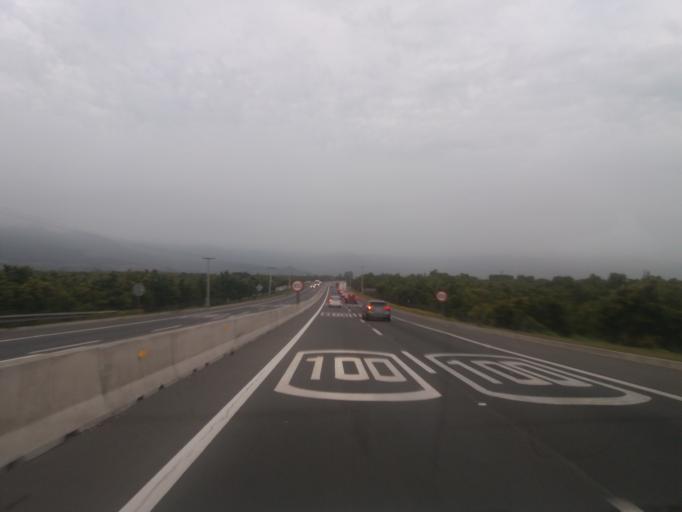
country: CL
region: Valparaiso
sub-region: Provincia de Quillota
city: Hacienda La Calera
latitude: -32.8269
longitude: -71.2230
